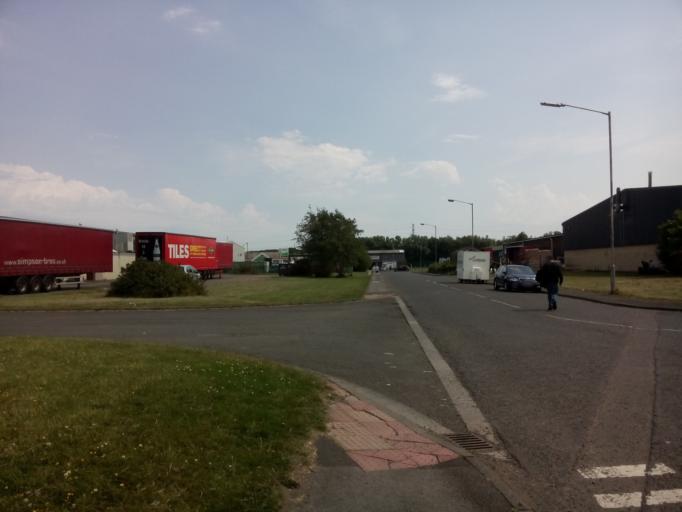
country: GB
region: England
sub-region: Northumberland
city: Backworth
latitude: 55.0224
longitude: -1.5425
